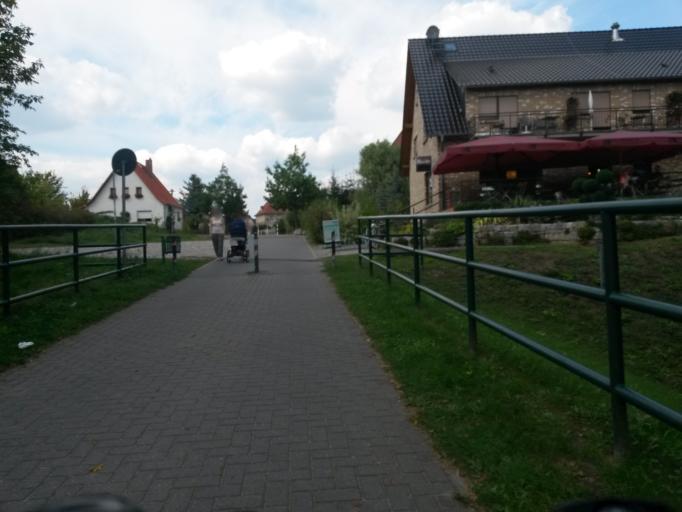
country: DE
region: Brandenburg
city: Templin
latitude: 53.1243
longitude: 13.5013
